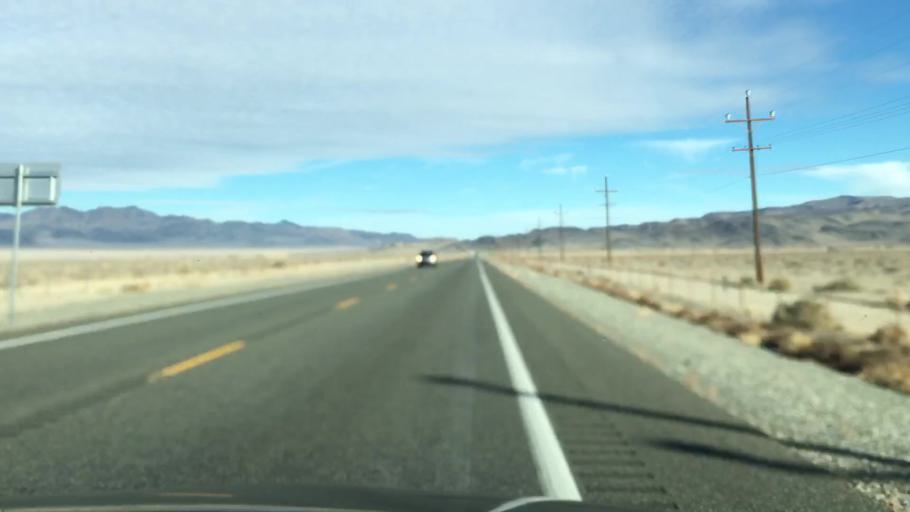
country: US
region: Nevada
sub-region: Mineral County
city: Hawthorne
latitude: 38.5255
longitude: -118.5724
